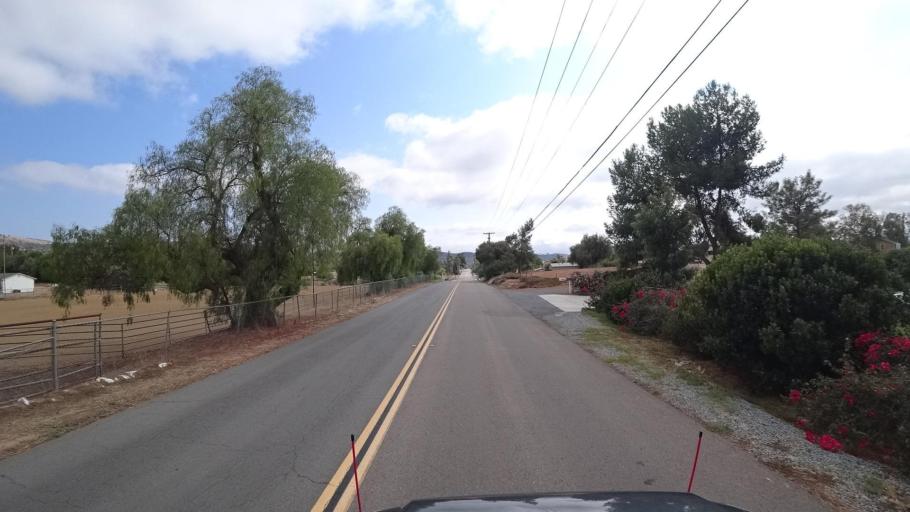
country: US
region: California
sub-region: San Diego County
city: Ramona
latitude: 33.0323
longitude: -116.8493
